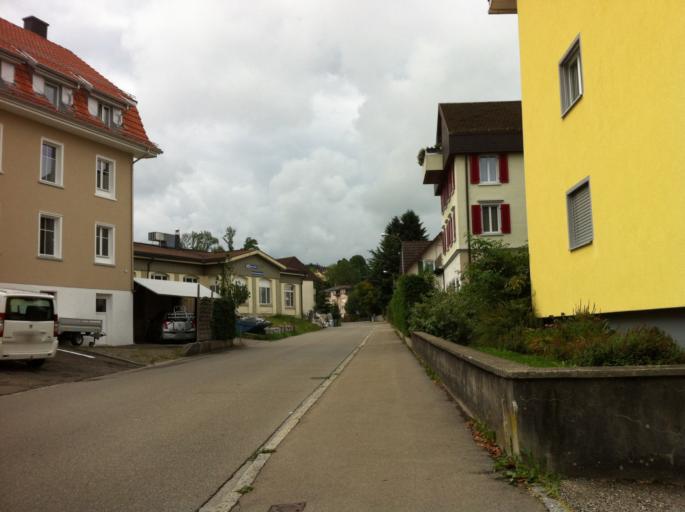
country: CH
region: Saint Gallen
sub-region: Wahlkreis St. Gallen
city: Gossau
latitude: 47.4102
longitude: 9.2485
